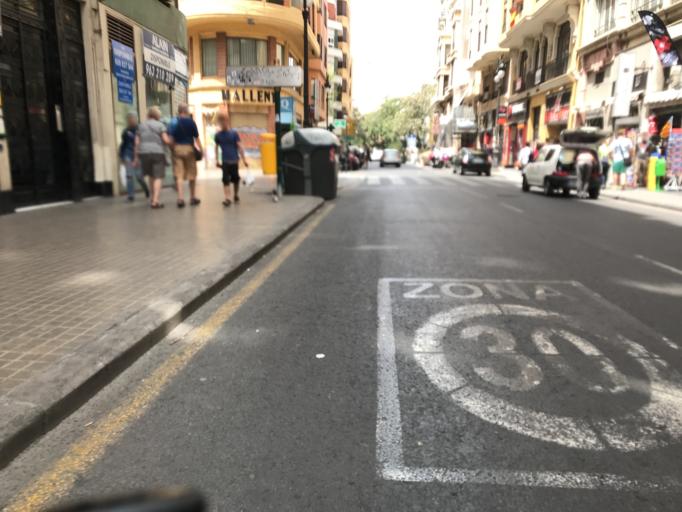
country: ES
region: Valencia
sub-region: Provincia de Valencia
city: Valencia
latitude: 39.4722
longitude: -0.3769
